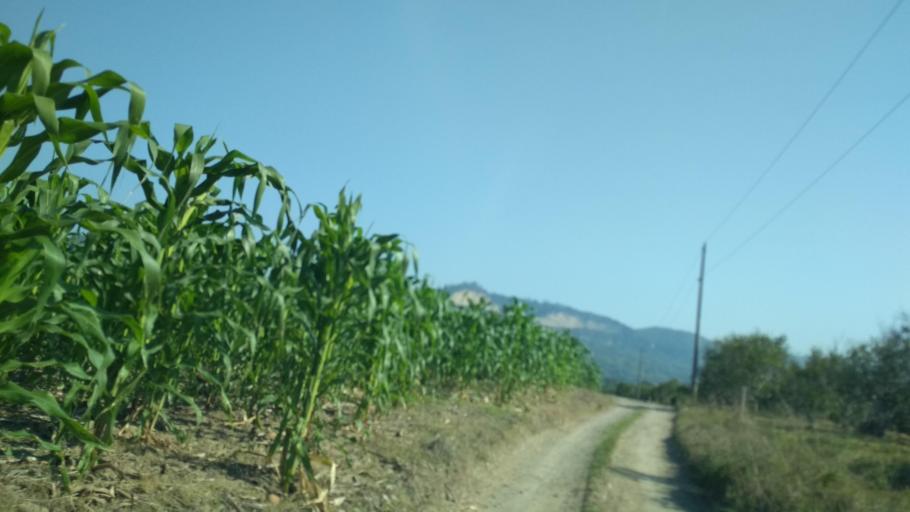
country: MX
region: Veracruz
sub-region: Papantla
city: Polutla
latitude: 20.4536
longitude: -97.2115
